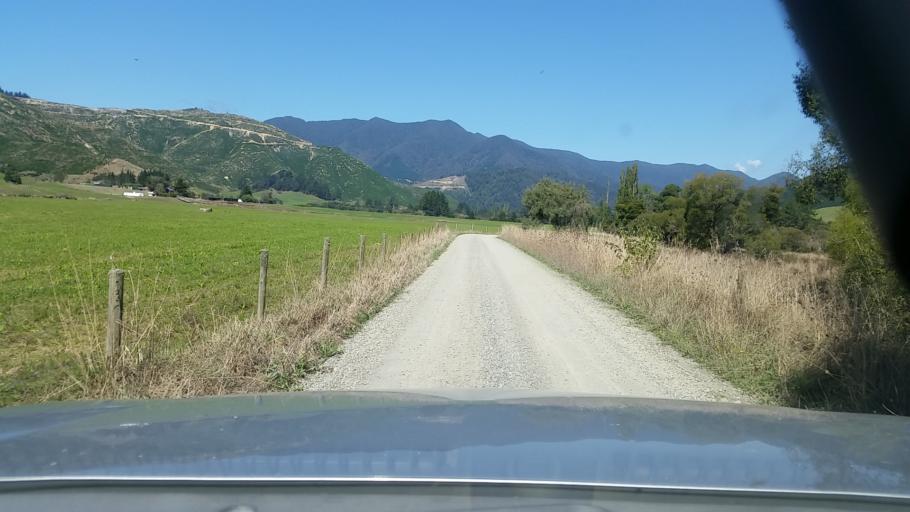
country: NZ
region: Nelson
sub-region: Nelson City
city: Nelson
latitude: -41.2653
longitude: 173.5763
